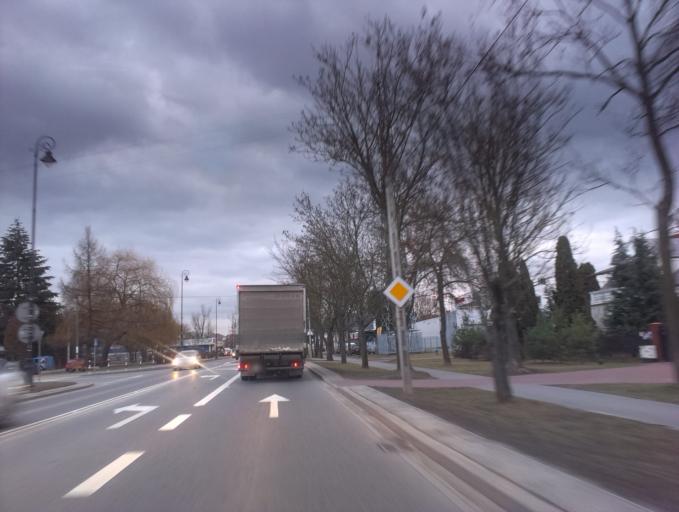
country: PL
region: Masovian Voivodeship
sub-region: Powiat piaseczynski
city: Konstancin-Jeziorna
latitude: 52.0984
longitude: 21.1159
